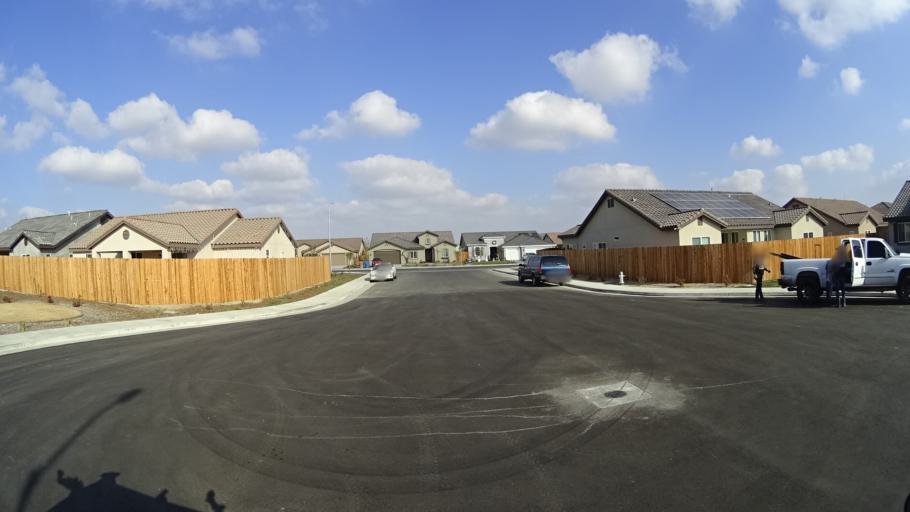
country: US
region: California
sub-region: Kern County
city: Greenacres
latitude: 35.2899
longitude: -119.1041
